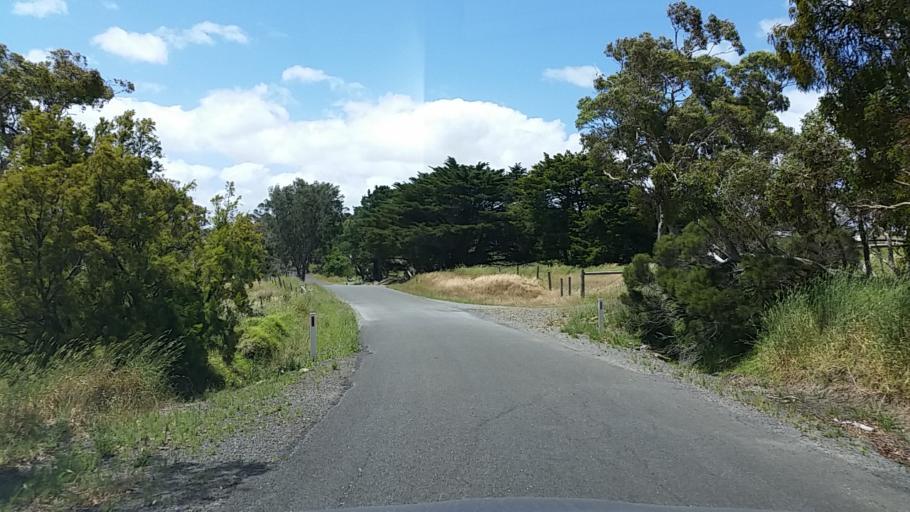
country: AU
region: South Australia
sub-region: Alexandrina
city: Mount Compass
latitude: -35.4424
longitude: 138.5941
